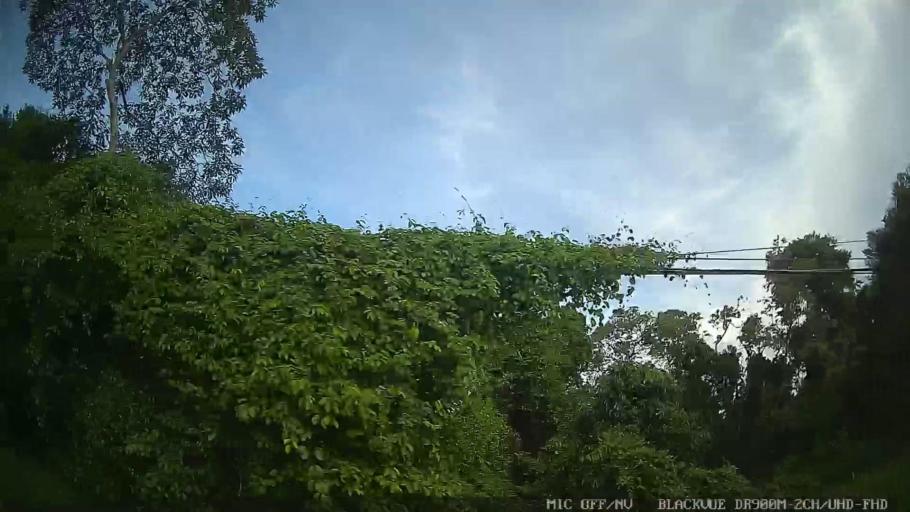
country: BR
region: Sao Paulo
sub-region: Serra Negra
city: Serra Negra
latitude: -22.6944
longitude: -46.6783
